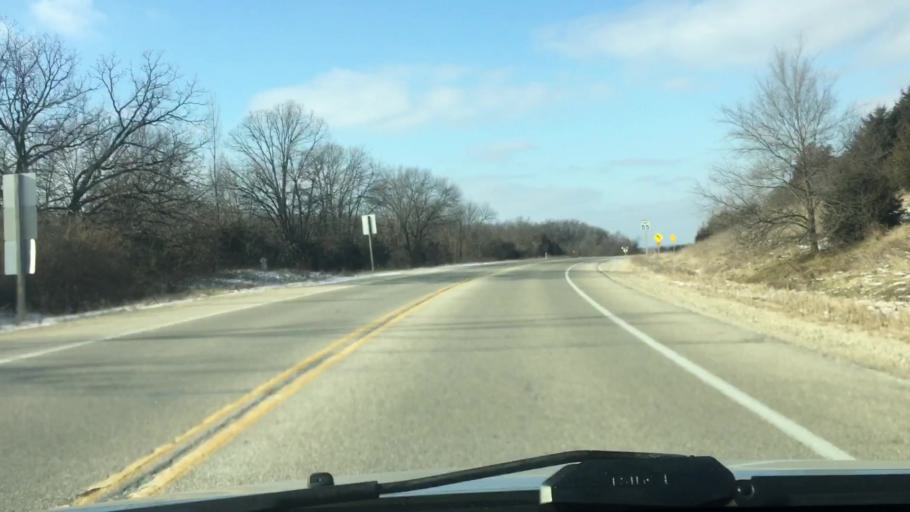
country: US
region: Wisconsin
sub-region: Waukesha County
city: Eagle
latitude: 42.8793
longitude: -88.4836
